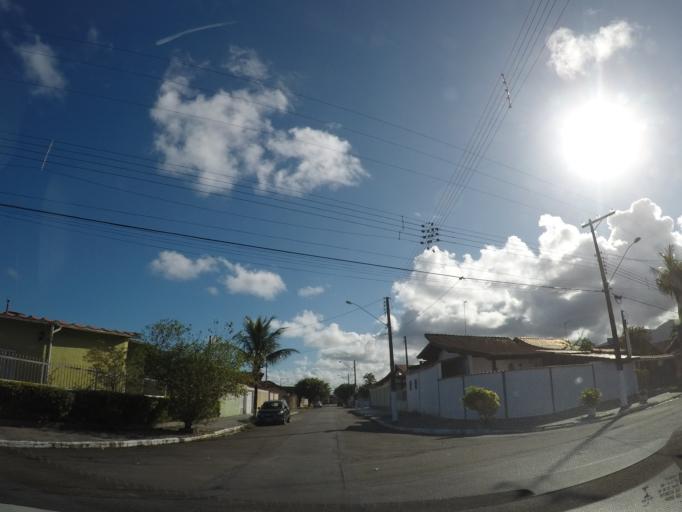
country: BR
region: Sao Paulo
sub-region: Mongagua
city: Mongagua
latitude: -24.0578
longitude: -46.5489
